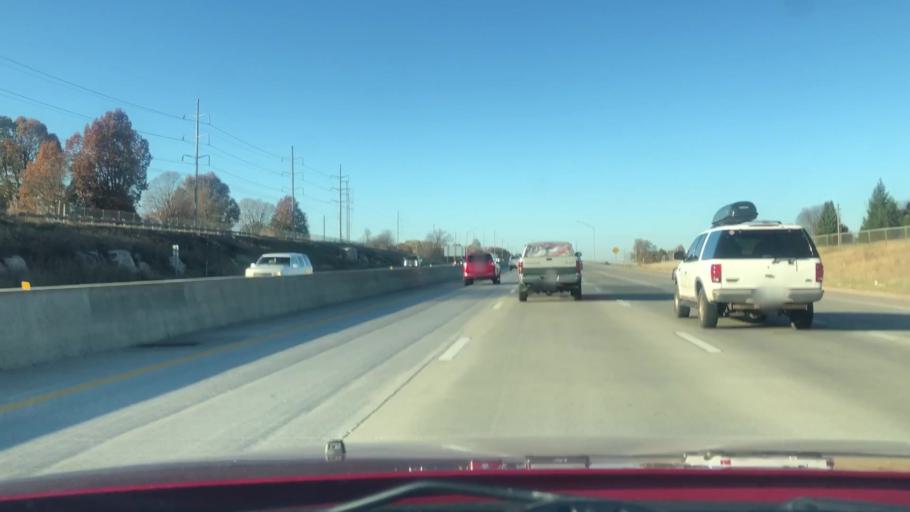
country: US
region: Missouri
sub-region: Greene County
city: Springfield
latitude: 37.1878
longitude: -93.2239
